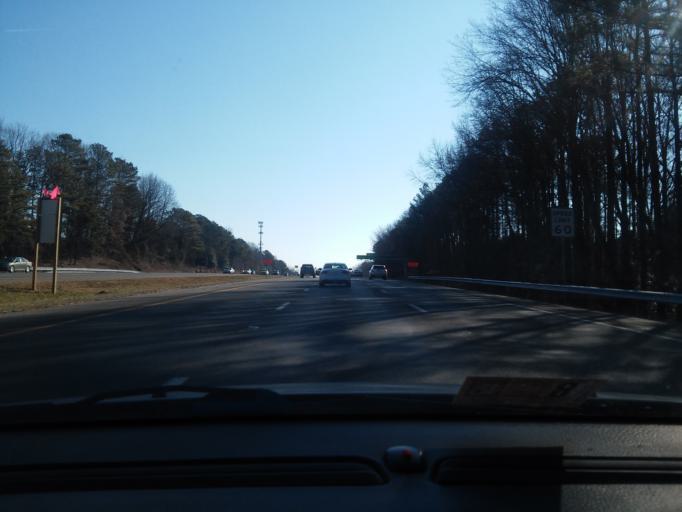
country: US
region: Virginia
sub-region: Henrico County
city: Tuckahoe
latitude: 37.6271
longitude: -77.5604
